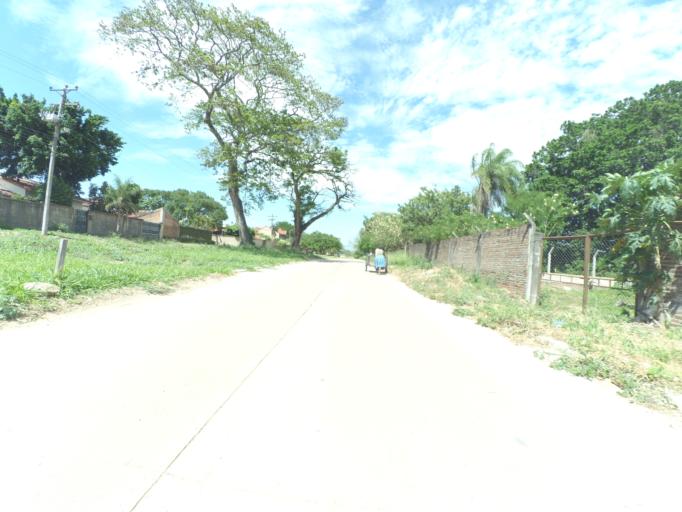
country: BO
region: Santa Cruz
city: Santa Cruz de la Sierra
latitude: -17.8084
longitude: -63.2292
